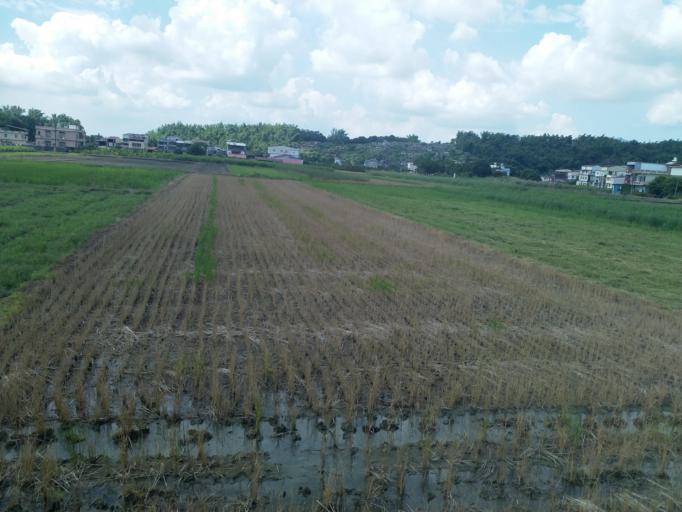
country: TW
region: Taiwan
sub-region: Pingtung
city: Pingtung
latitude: 22.8797
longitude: 120.5753
